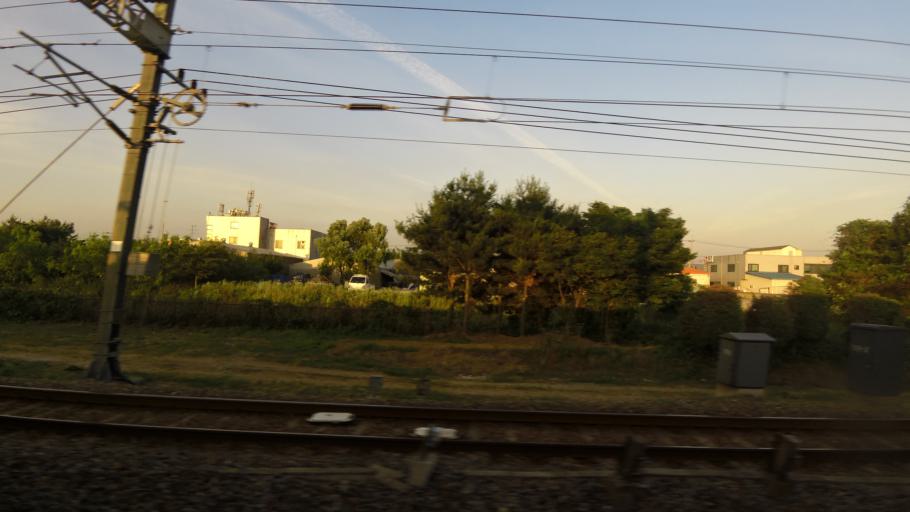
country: KR
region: Chungcheongnam-do
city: Seonghwan
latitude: 37.0172
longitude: 127.0706
